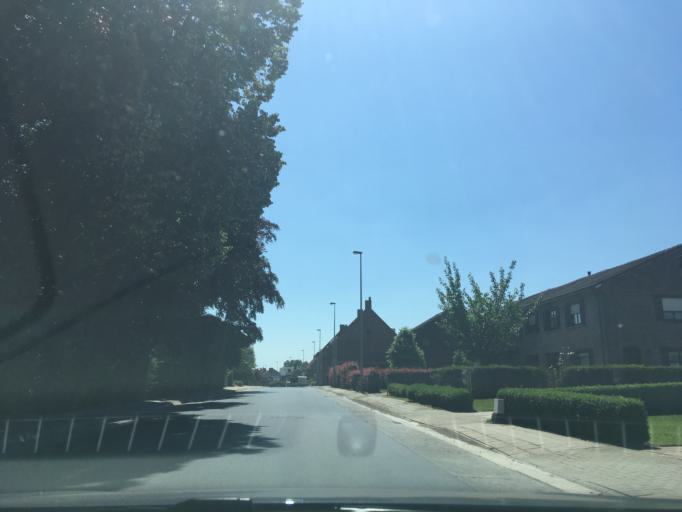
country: BE
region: Flanders
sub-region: Provincie West-Vlaanderen
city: Ardooie
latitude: 51.0059
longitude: 3.2081
